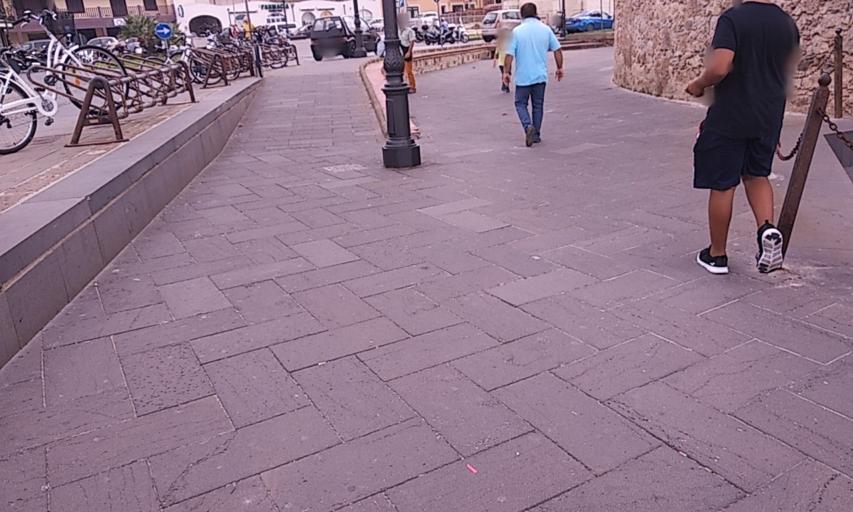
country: IT
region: Sardinia
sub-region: Provincia di Sassari
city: Alghero
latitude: 40.5563
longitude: 8.3151
